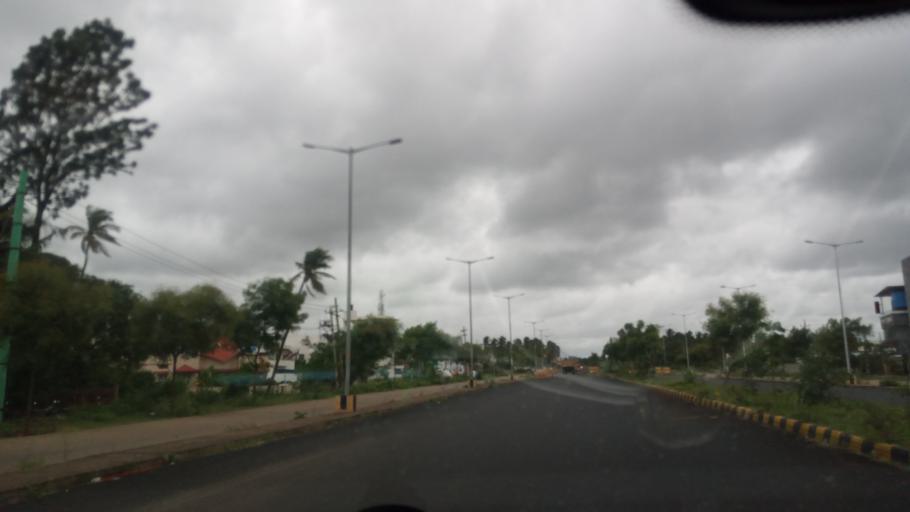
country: IN
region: Karnataka
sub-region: Mysore
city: Mysore
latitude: 12.2907
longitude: 76.6057
